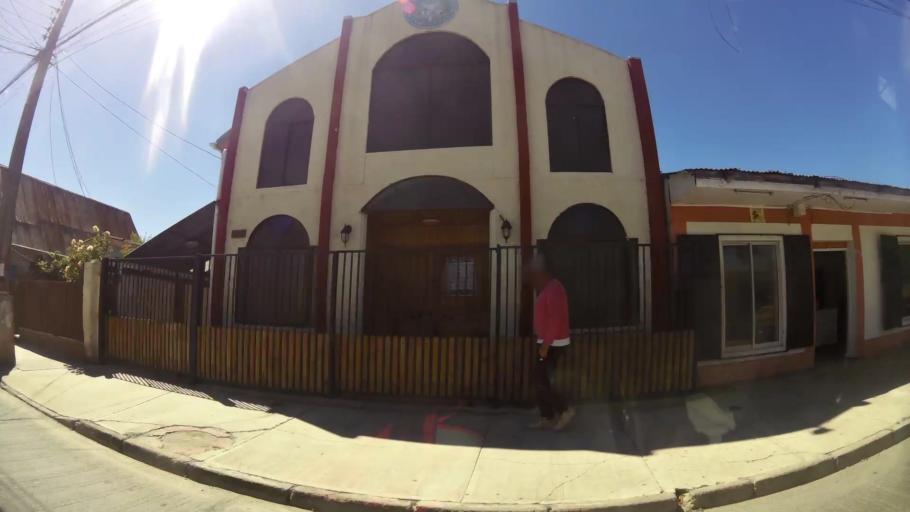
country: CL
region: Valparaiso
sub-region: Provincia de Marga Marga
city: Quilpue
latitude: -33.3193
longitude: -71.4062
